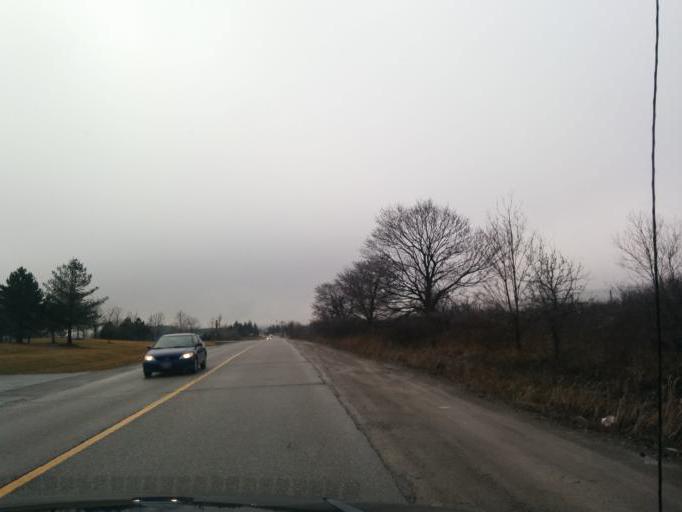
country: CA
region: Ontario
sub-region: Halton
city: Milton
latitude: 43.5257
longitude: -79.9094
